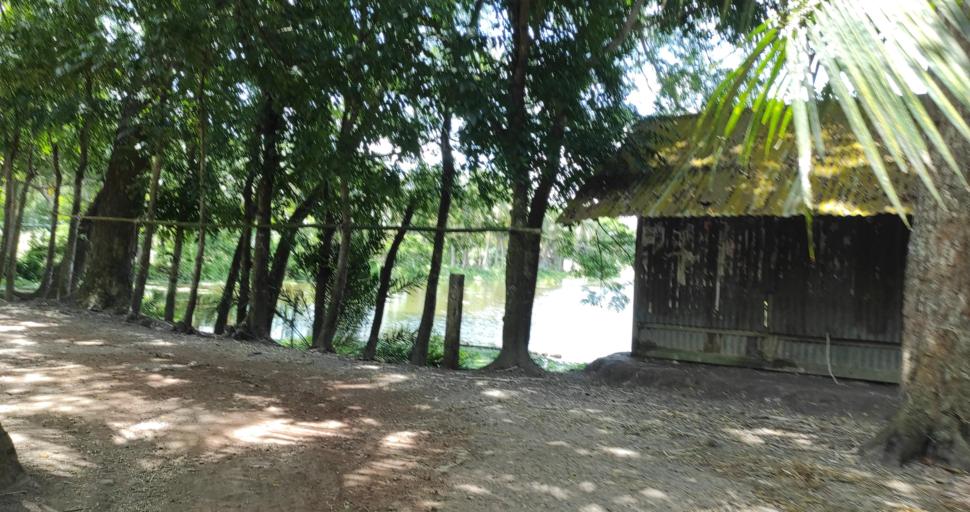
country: BD
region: Barisal
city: Gaurnadi
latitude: 22.9176
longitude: 90.0824
